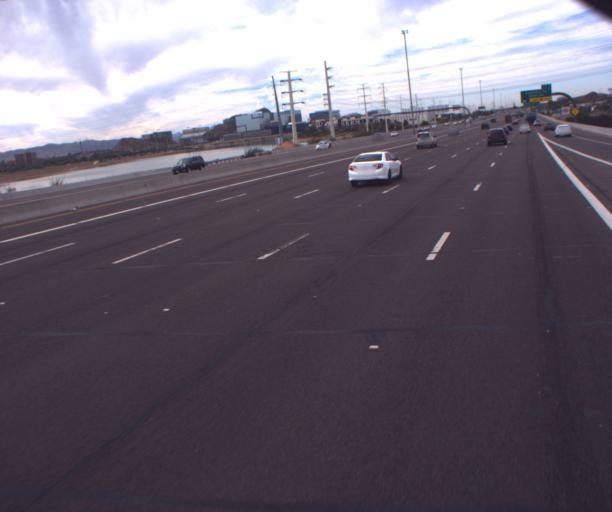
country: US
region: Arizona
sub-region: Maricopa County
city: Tempe
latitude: 33.4362
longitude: -111.9134
